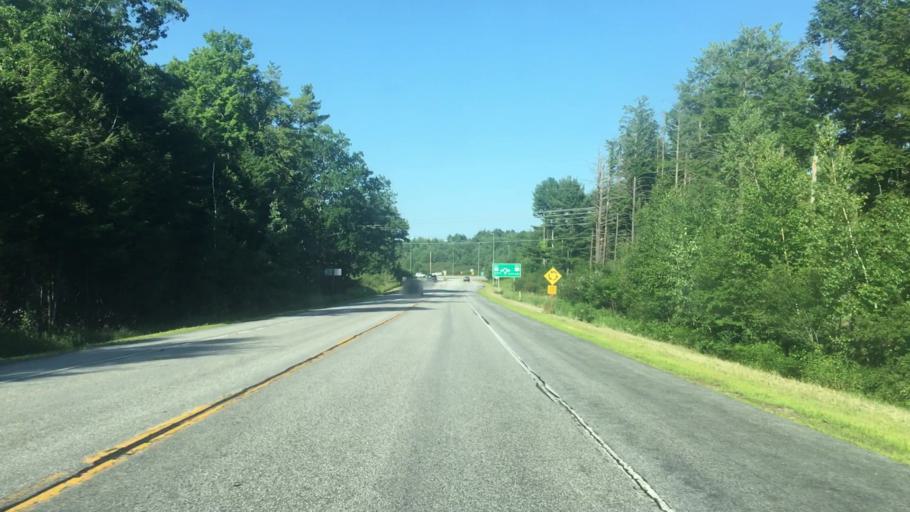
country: US
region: Maine
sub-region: Cumberland County
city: Gorham
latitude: 43.6508
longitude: -70.4316
